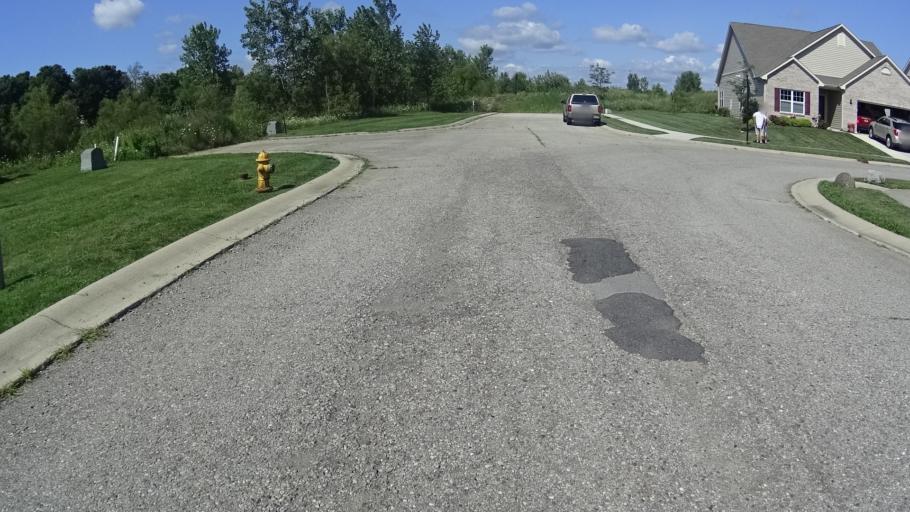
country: US
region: Indiana
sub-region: Madison County
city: Pendleton
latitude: 39.9799
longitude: -85.7468
